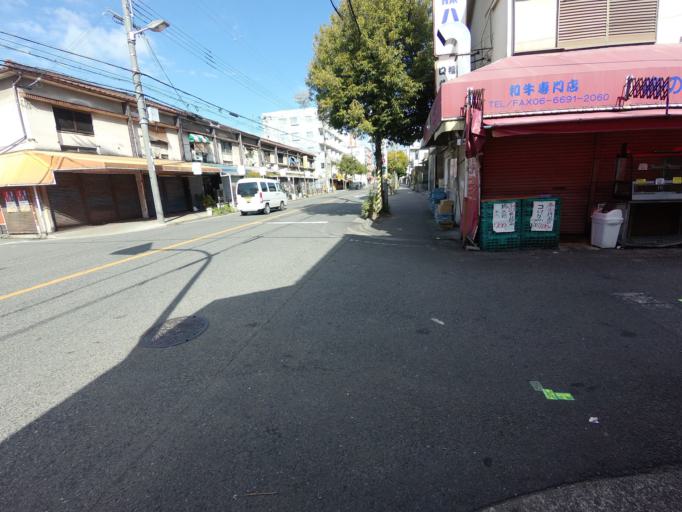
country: JP
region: Osaka
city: Sakai
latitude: 34.5951
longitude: 135.5026
